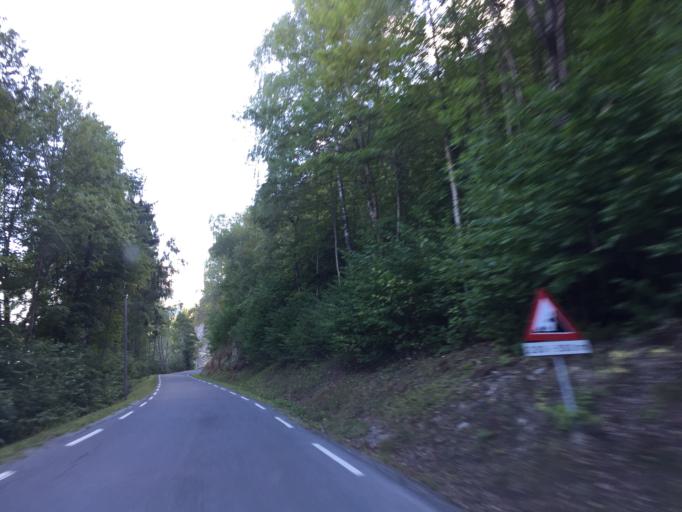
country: NO
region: Buskerud
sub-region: Ovre Eiker
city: Hokksund
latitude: 59.6816
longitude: 9.8592
